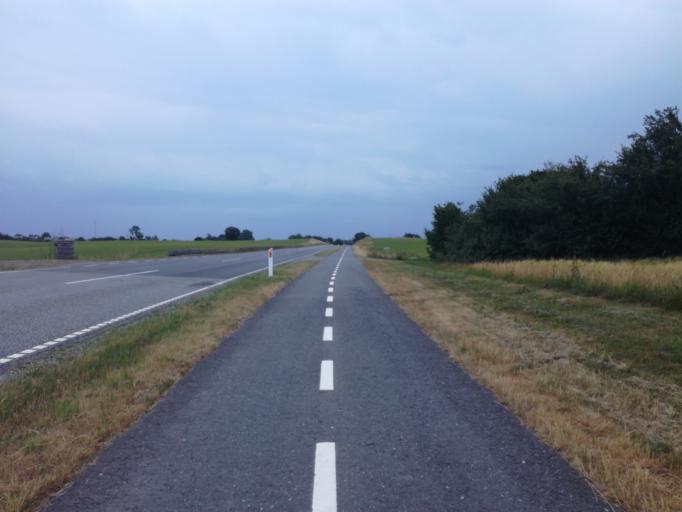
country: DK
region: South Denmark
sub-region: Vejle Kommune
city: Borkop
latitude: 55.6722
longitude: 9.6170
